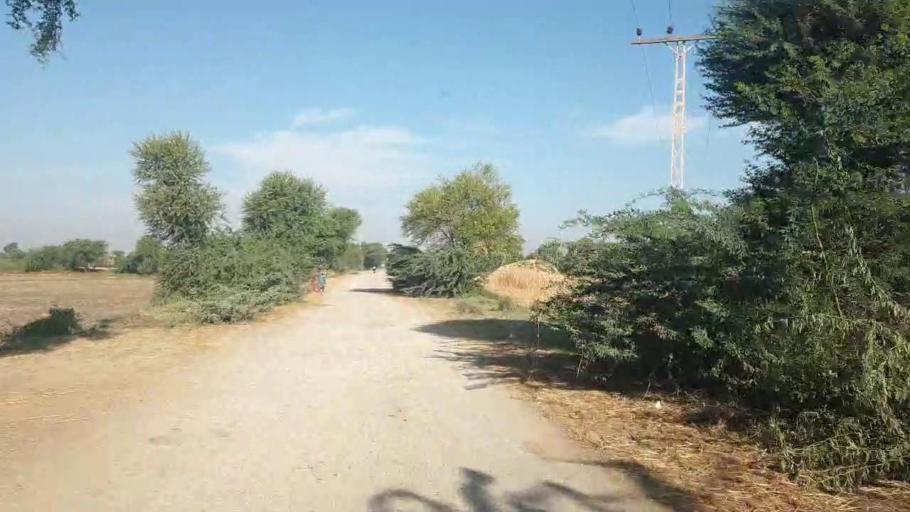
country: PK
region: Sindh
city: Talhar
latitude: 24.9428
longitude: 68.7880
